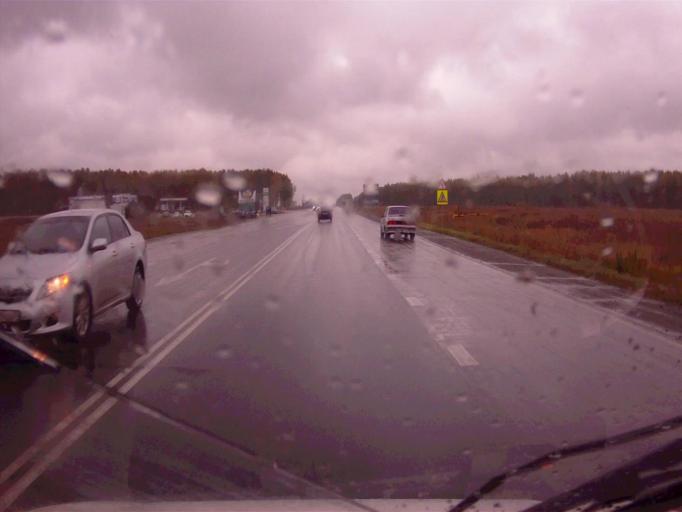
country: RU
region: Chelyabinsk
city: Argayash
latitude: 55.4165
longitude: 61.0276
